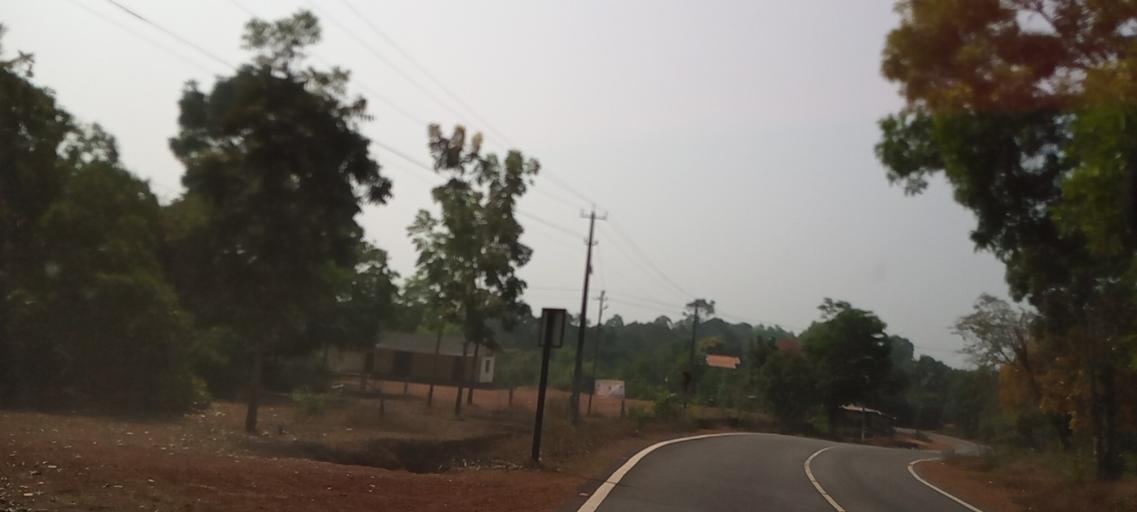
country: IN
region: Karnataka
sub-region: Udupi
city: Someshwar
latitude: 13.5357
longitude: 74.9163
